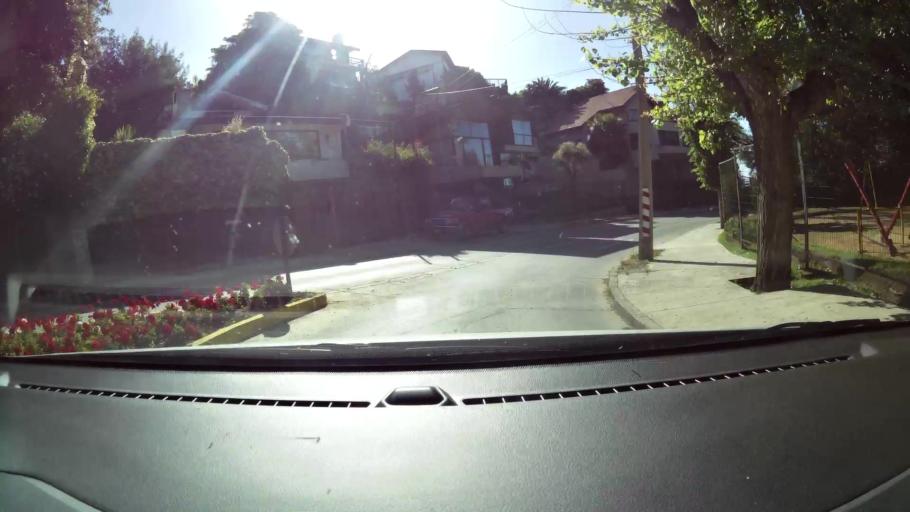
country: CL
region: Valparaiso
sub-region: Provincia de Valparaiso
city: Vina del Mar
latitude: -33.0346
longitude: -71.5567
